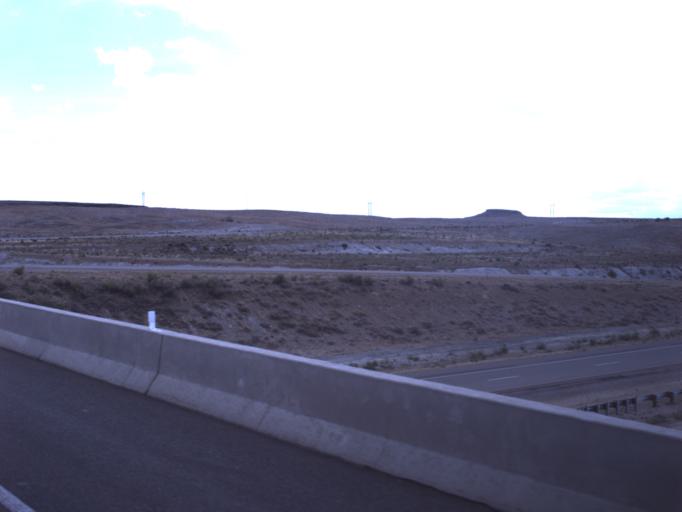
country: US
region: Utah
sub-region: Carbon County
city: East Carbon City
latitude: 38.9764
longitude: -110.1213
